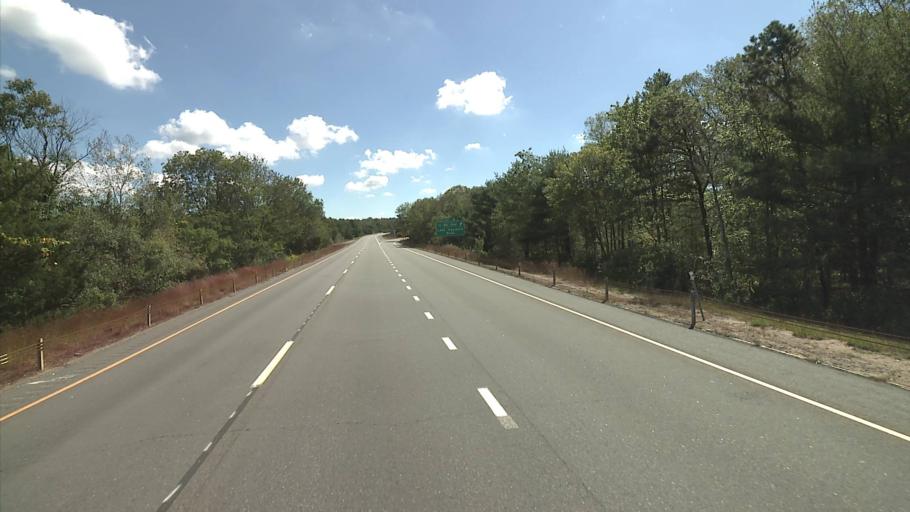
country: US
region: Connecticut
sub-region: New London County
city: Colchester
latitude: 41.5618
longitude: -72.3262
